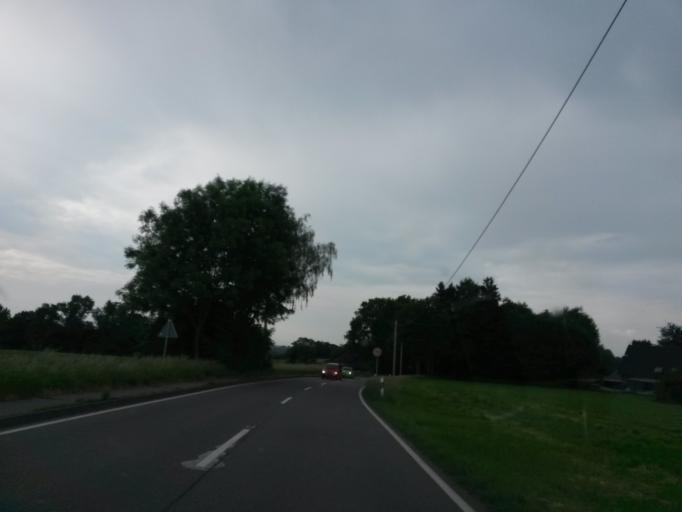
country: DE
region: North Rhine-Westphalia
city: Lohmar
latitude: 50.8690
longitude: 7.2290
